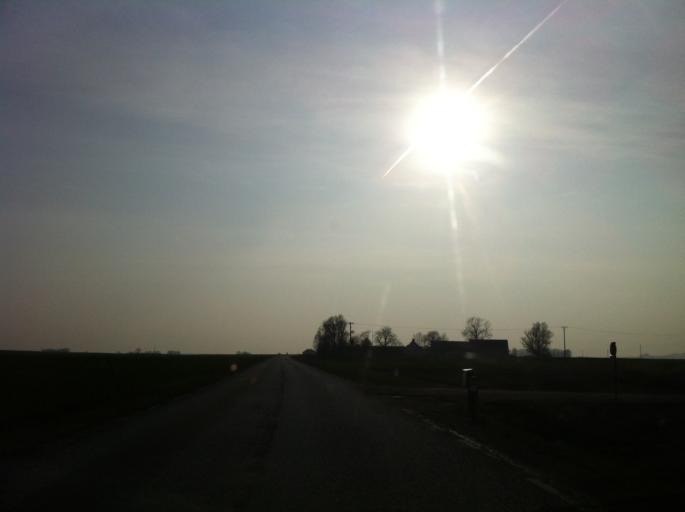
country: SE
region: Skane
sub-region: Svalovs Kommun
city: Svaloev
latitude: 55.9082
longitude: 13.0942
